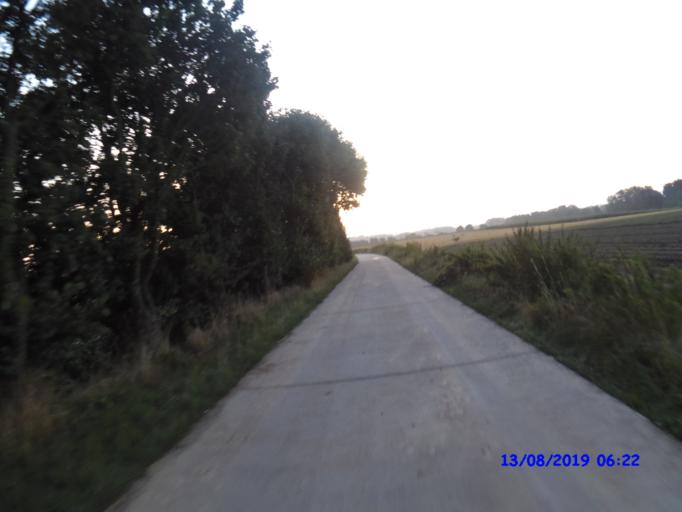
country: BE
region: Flanders
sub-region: Provincie Vlaams-Brabant
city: Asse
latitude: 50.9246
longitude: 4.2129
